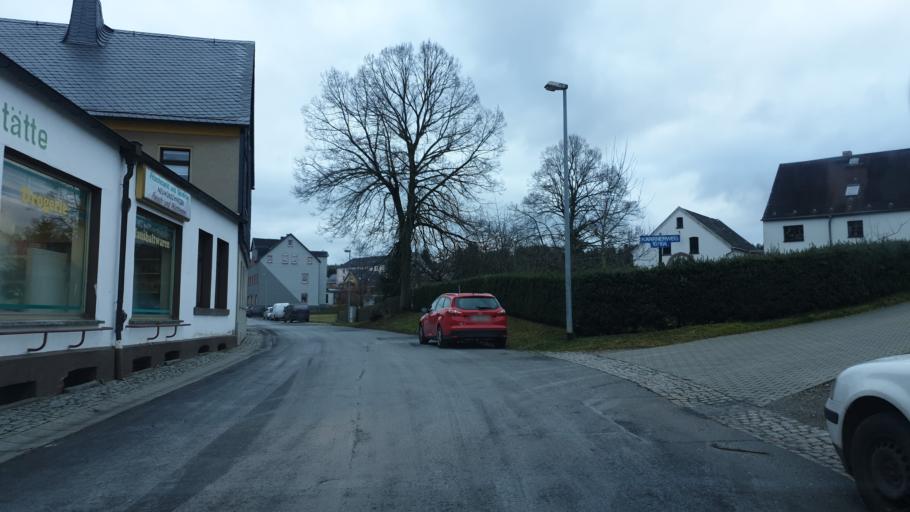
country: DE
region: Saxony
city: Hohndorf
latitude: 50.7310
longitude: 12.6652
